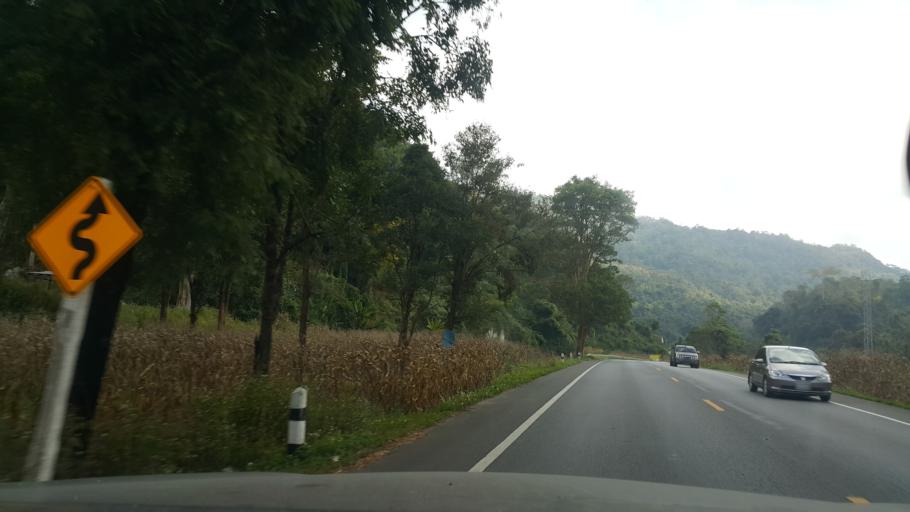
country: TH
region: Lampang
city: Wang Nuea
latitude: 19.0640
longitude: 99.7478
